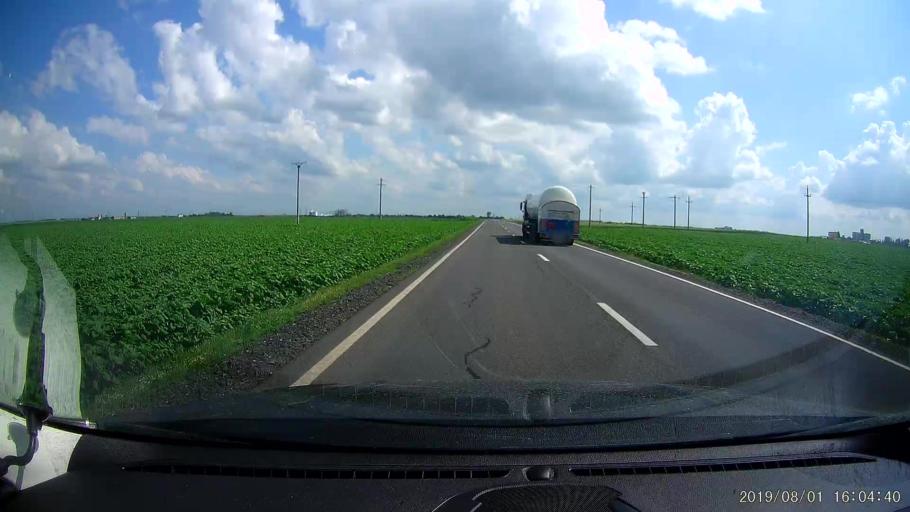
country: RO
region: Calarasi
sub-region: Comuna Dragalina
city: Drajna Noua
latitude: 44.4413
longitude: 27.3790
